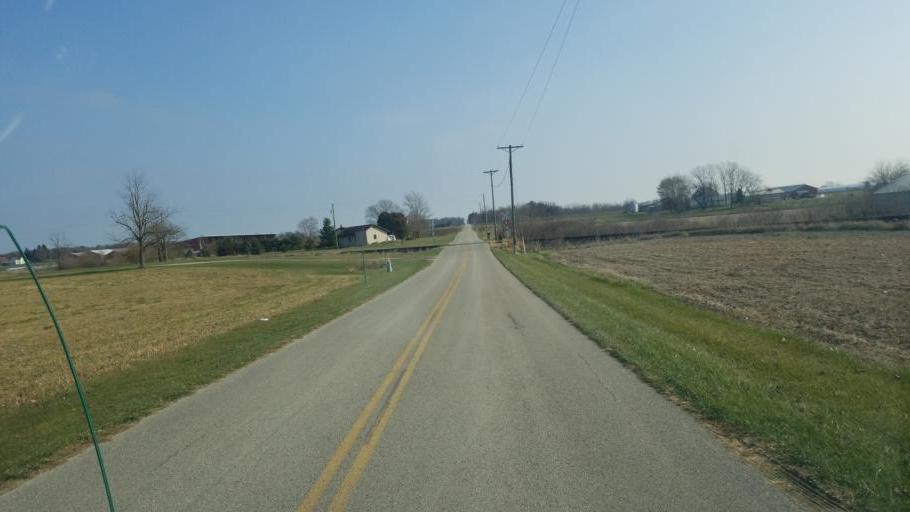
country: US
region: Ohio
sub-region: Mercer County
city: Fort Recovery
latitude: 40.4286
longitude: -84.7349
